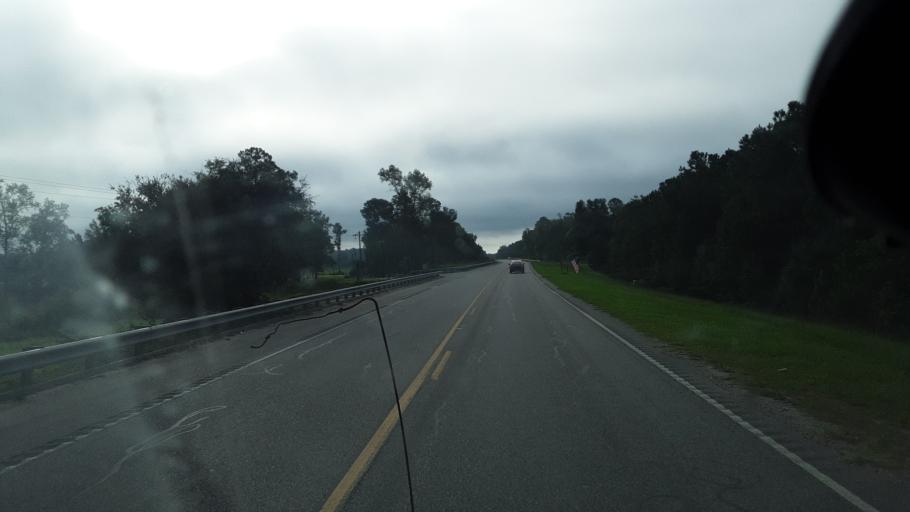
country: US
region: South Carolina
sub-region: Horry County
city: Red Hill
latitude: 33.8449
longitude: -79.2819
